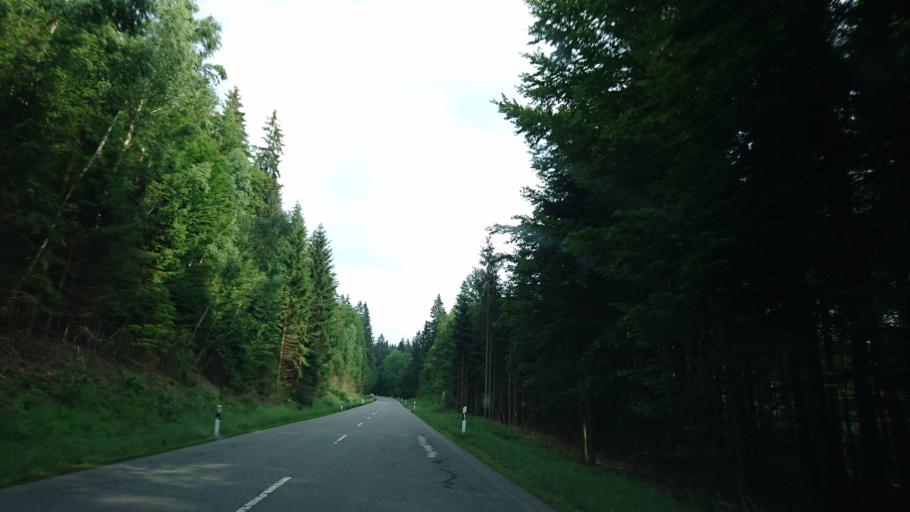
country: DE
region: Bavaria
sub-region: Lower Bavaria
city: Neuschonau
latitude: 48.9164
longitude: 13.4563
